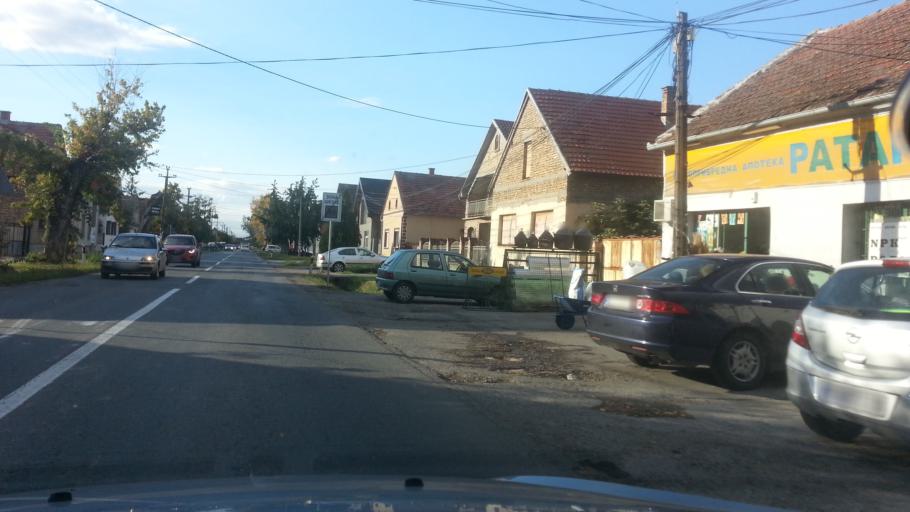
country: RS
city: Novi Banovci
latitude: 44.9072
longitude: 20.2731
